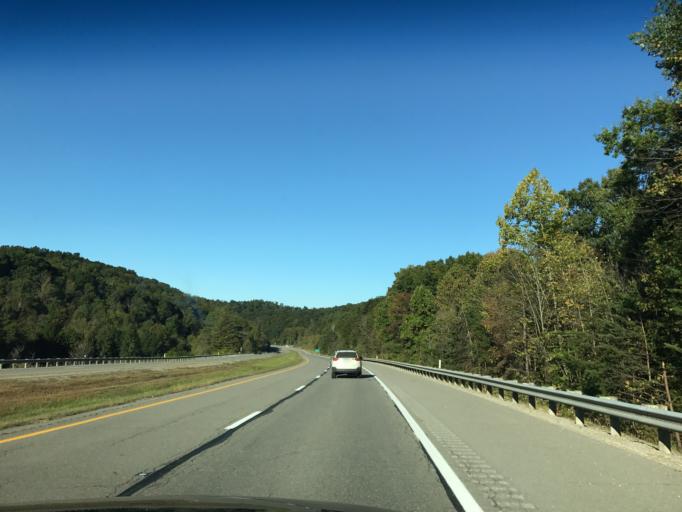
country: US
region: Ohio
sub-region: Washington County
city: Newport
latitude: 39.2590
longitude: -81.2809
